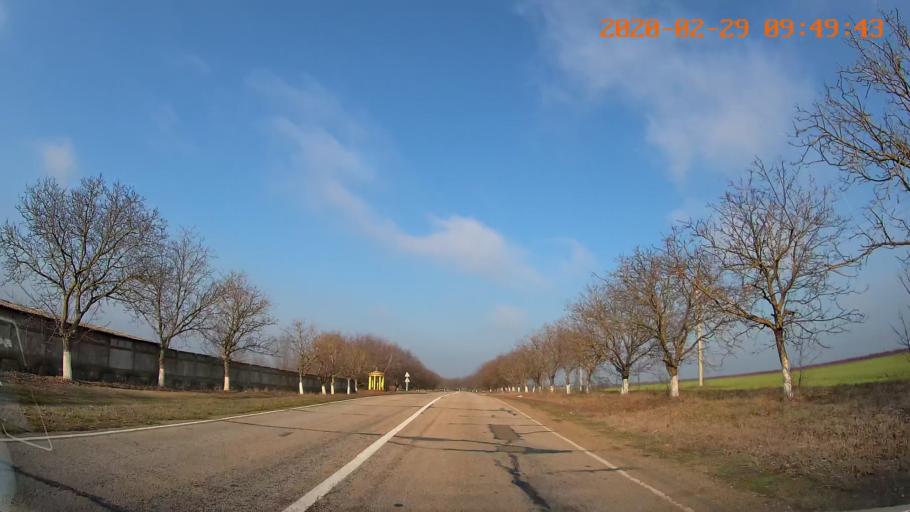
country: MD
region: Telenesti
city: Crasnoe
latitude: 46.6990
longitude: 29.7680
